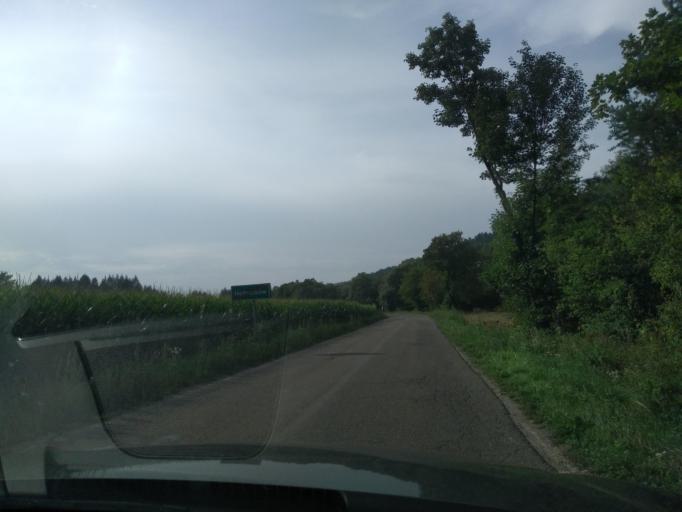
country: PL
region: Subcarpathian Voivodeship
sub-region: Powiat sanocki
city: Tyrawa Woloska
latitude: 49.5923
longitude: 22.3371
